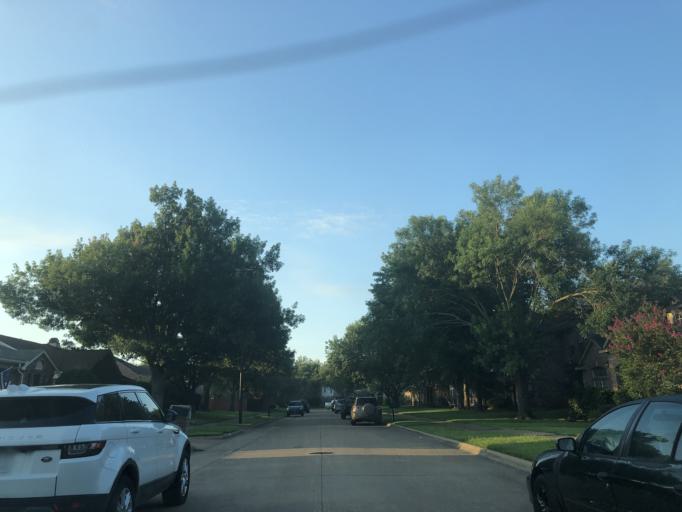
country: US
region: Texas
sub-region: Dallas County
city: Sunnyvale
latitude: 32.8383
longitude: -96.5631
